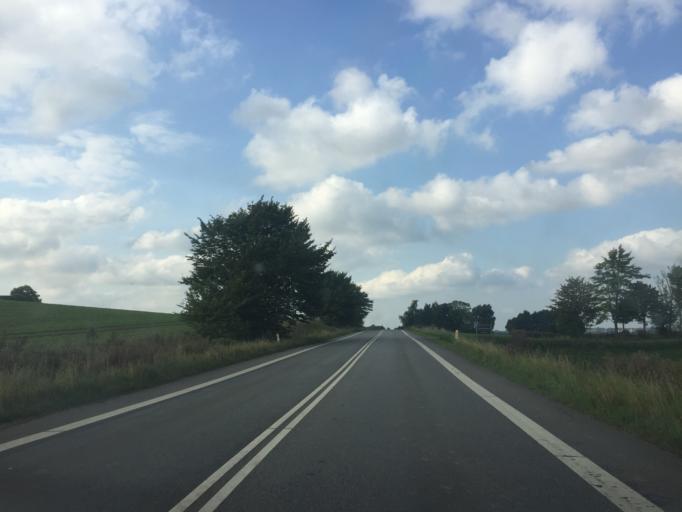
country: DK
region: Zealand
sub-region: Holbaek Kommune
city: Tollose
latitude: 55.6361
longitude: 11.7892
